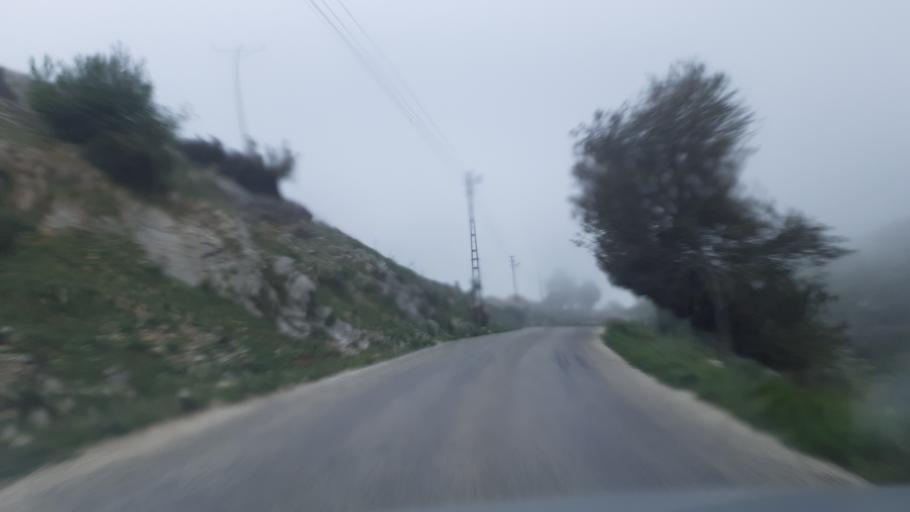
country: TR
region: Hatay
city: Yeditepe
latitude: 35.9680
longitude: 36.0077
